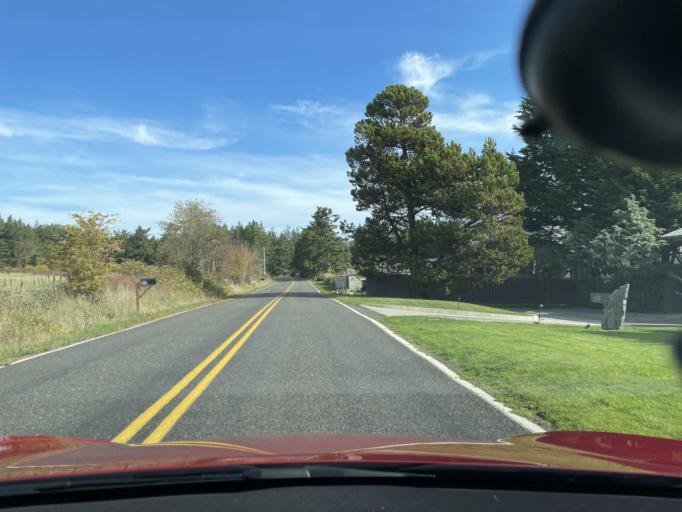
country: US
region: Washington
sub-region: San Juan County
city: Friday Harbor
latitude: 48.5199
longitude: -122.9782
